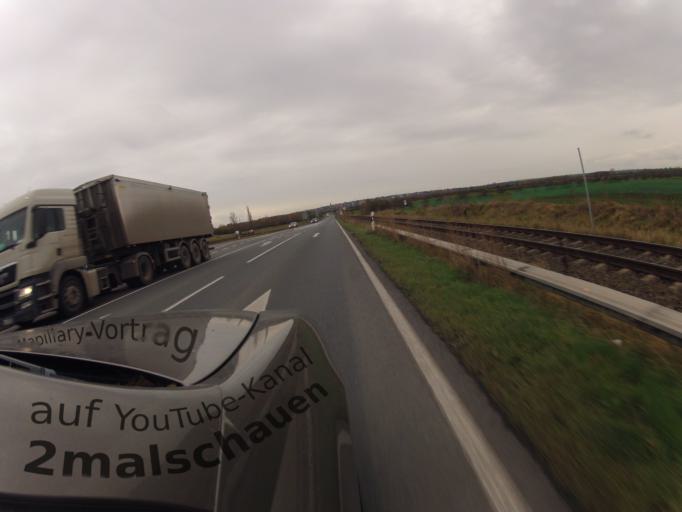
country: DE
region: Saxony-Anhalt
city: Konnern
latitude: 51.6898
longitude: 11.7666
